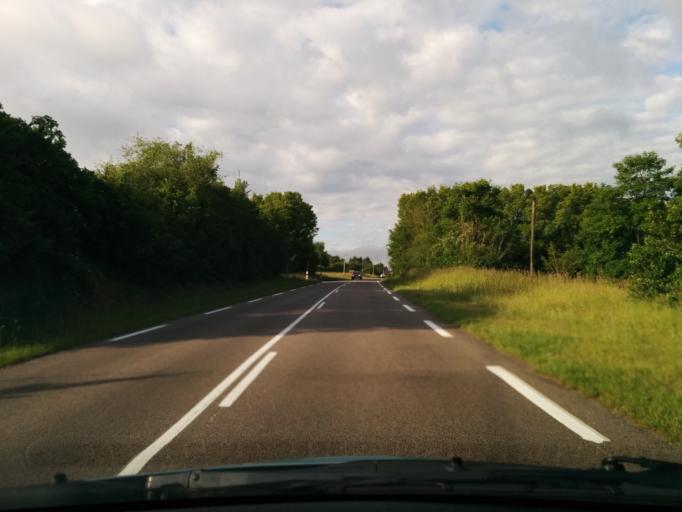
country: FR
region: Ile-de-France
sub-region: Departement des Yvelines
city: Follainville-Dennemont
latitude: 49.0469
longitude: 1.6909
